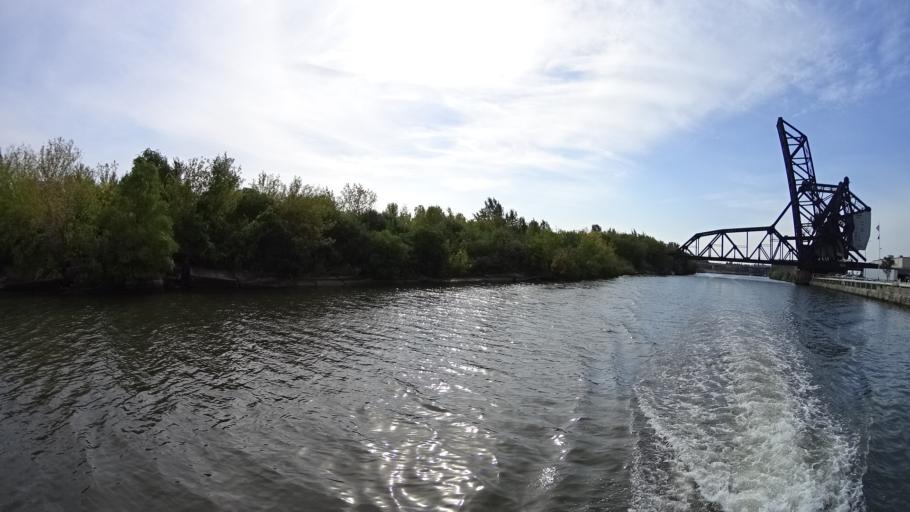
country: US
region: Illinois
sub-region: Cook County
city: Chicago
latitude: 41.8627
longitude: -87.6346
